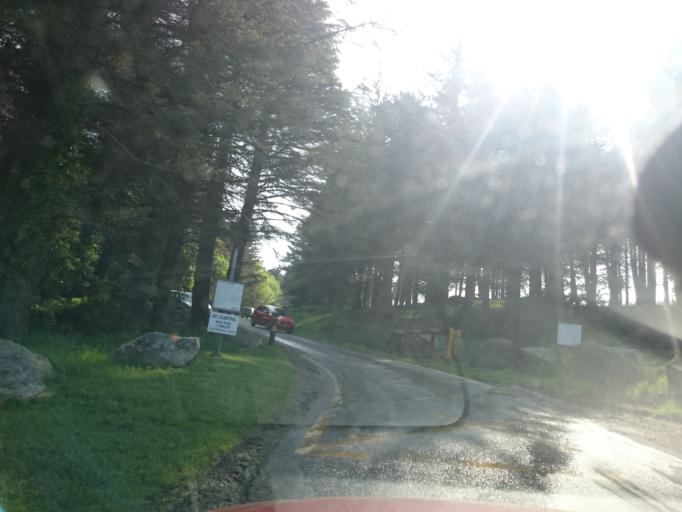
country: IE
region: Leinster
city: Ballinteer
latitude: 53.2556
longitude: -6.2512
